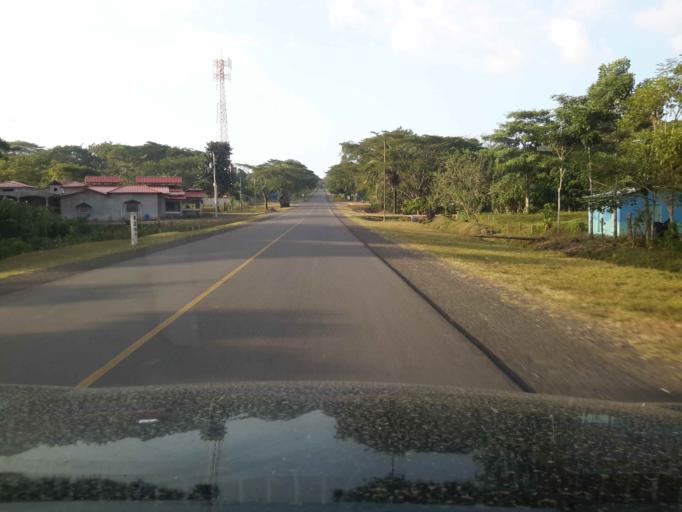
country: NI
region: Rio San Juan
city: San Miguelito
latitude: 11.3548
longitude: -84.7612
